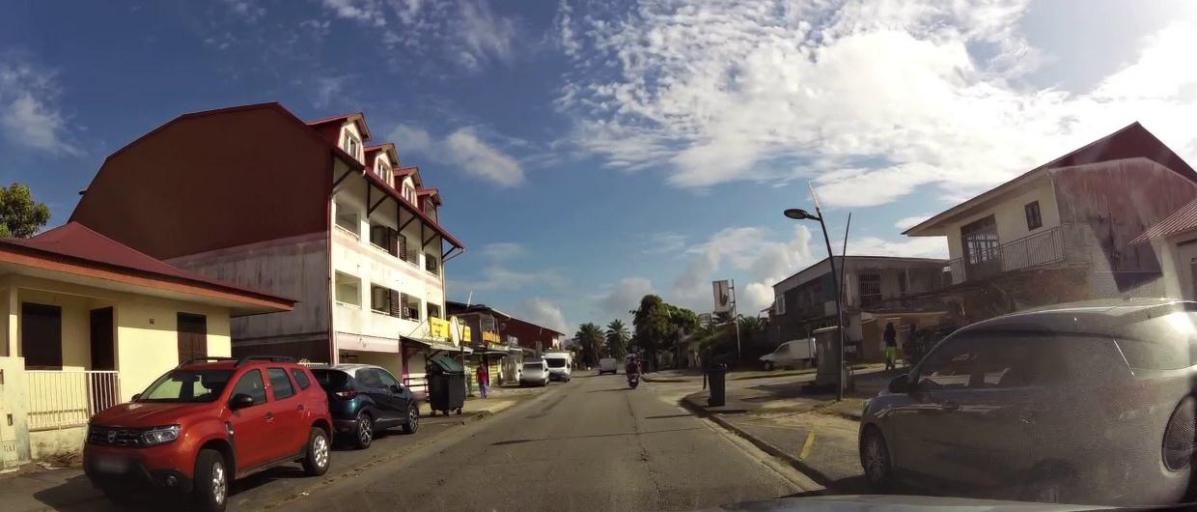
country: GF
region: Guyane
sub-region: Guyane
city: Kourou
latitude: 5.1561
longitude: -52.6432
